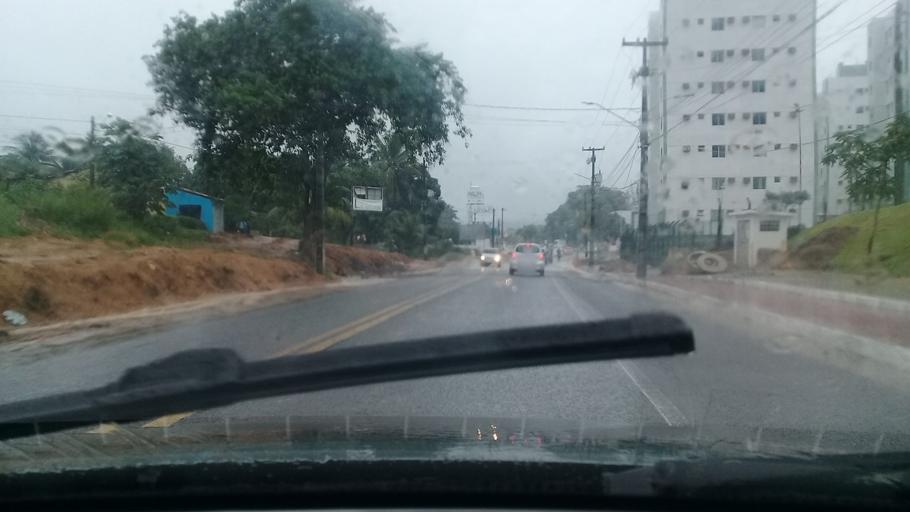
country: BR
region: Pernambuco
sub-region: Paulista
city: Paulista
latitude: -7.9484
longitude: -34.8882
